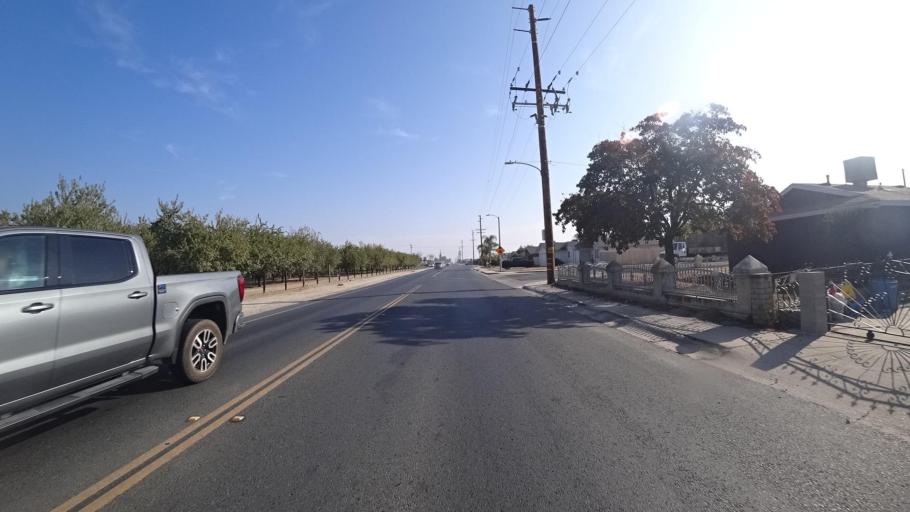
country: US
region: California
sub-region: Kern County
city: Delano
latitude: 35.7901
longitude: -119.2351
